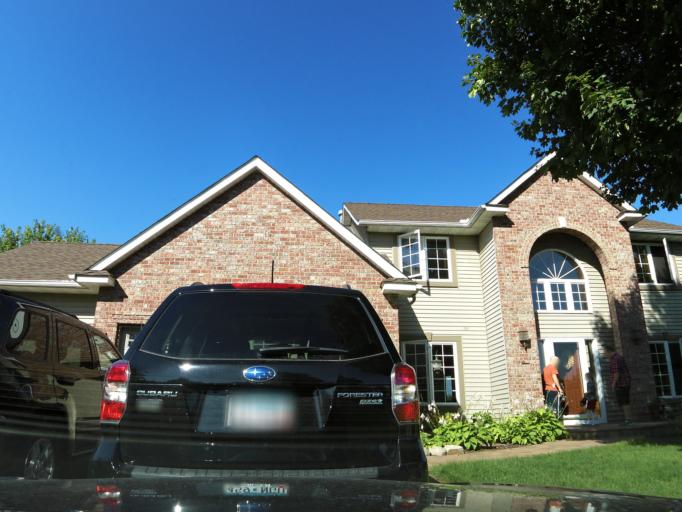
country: US
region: Minnesota
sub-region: Scott County
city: Savage
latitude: 44.7295
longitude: -93.3450
